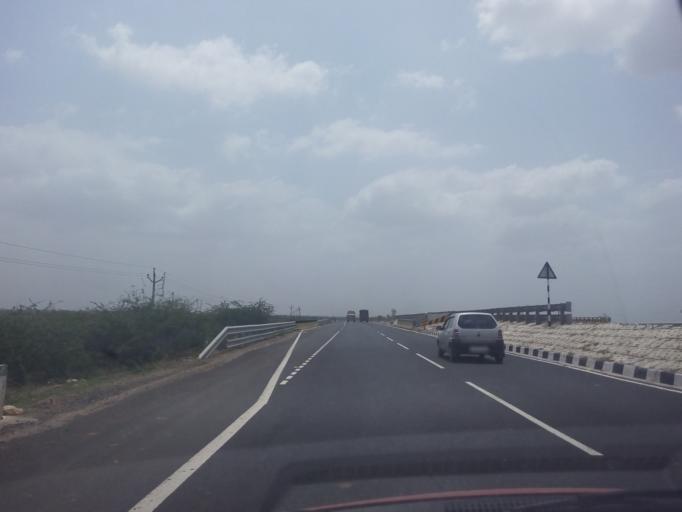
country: IN
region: Gujarat
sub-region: Surendranagar
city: Lakhtar
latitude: 23.0795
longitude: 71.8298
